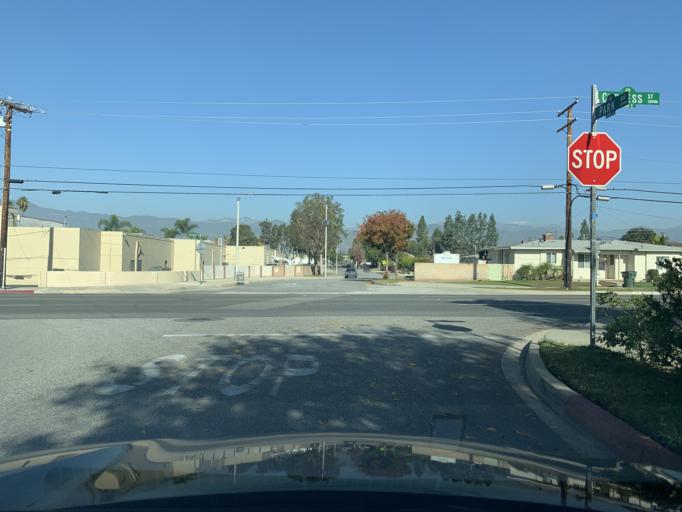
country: US
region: California
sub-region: Los Angeles County
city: Covina
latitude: 34.0955
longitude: -117.8893
